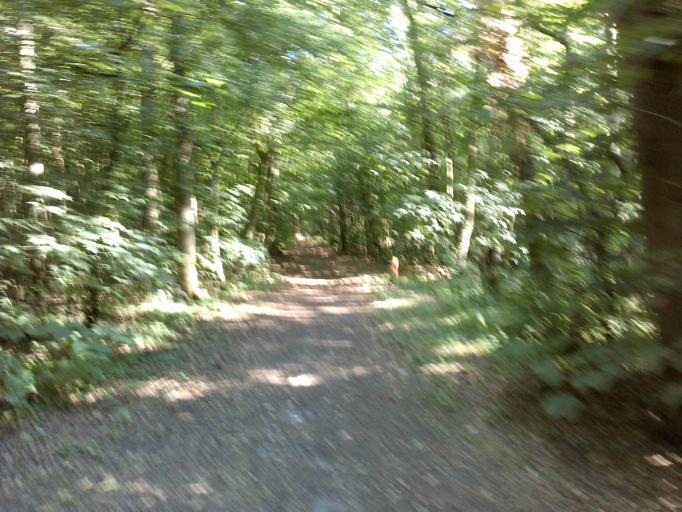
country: NL
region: South Holland
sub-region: Gemeente Hellevoetsluis
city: Nieuw-Helvoet
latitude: 51.8991
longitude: 4.0667
